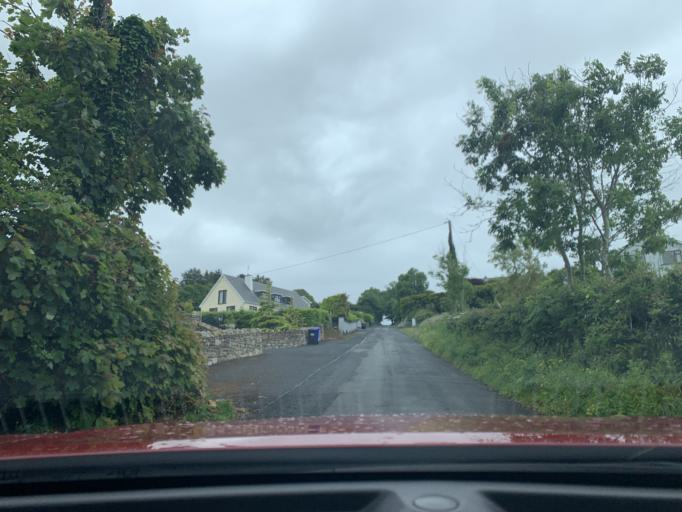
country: IE
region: Connaught
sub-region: Sligo
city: Sligo
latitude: 54.3145
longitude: -8.4782
